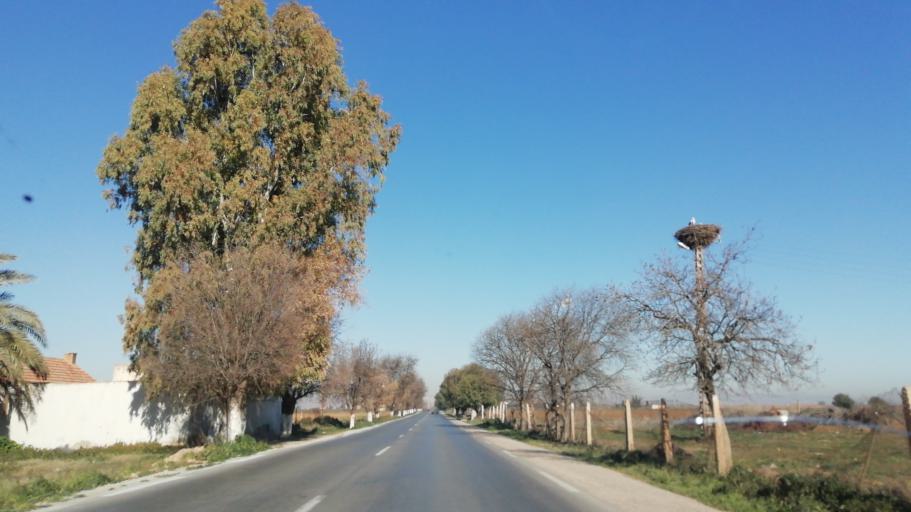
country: DZ
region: Mascara
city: Mascara
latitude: 35.2855
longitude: 0.1279
